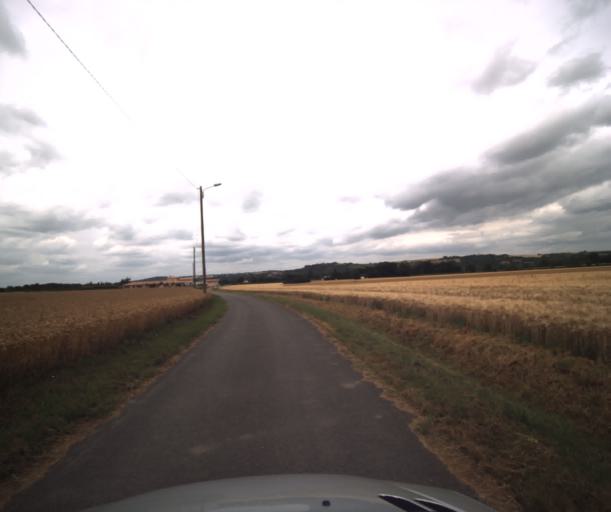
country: FR
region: Midi-Pyrenees
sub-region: Departement de la Haute-Garonne
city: Labarthe-sur-Leze
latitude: 43.4469
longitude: 1.4121
